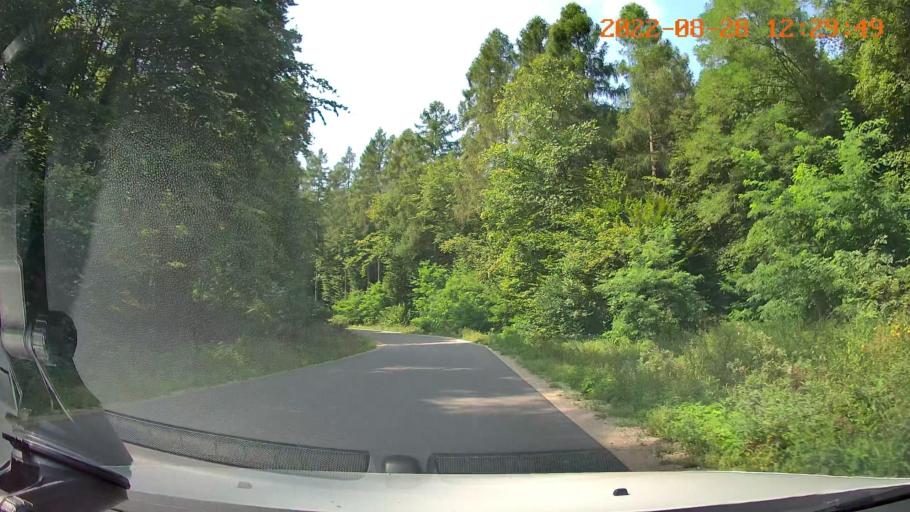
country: PL
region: Swietokrzyskie
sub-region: Powiat pinczowski
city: Michalow
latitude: 50.4139
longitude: 20.4621
